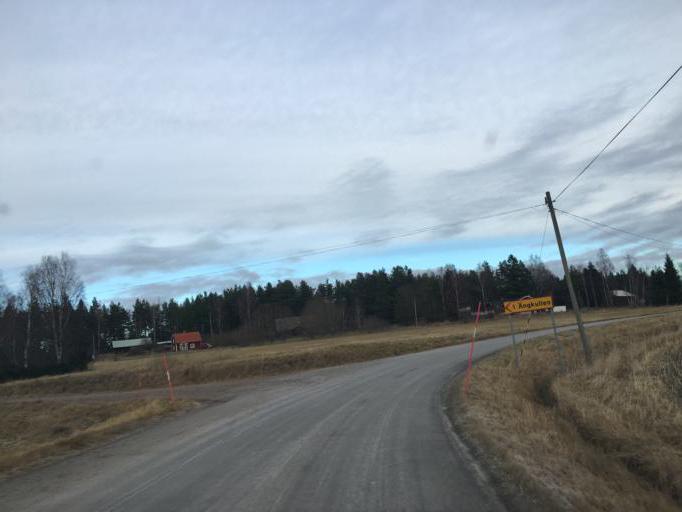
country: SE
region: OEstergoetland
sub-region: Norrkopings Kommun
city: Kimstad
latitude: 58.4269
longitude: 16.0642
